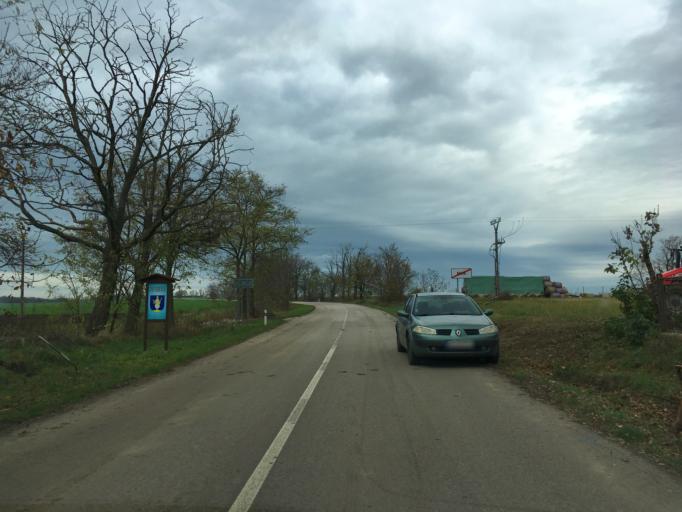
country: SK
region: Nitriansky
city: Svodin
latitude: 48.0223
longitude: 18.4067
